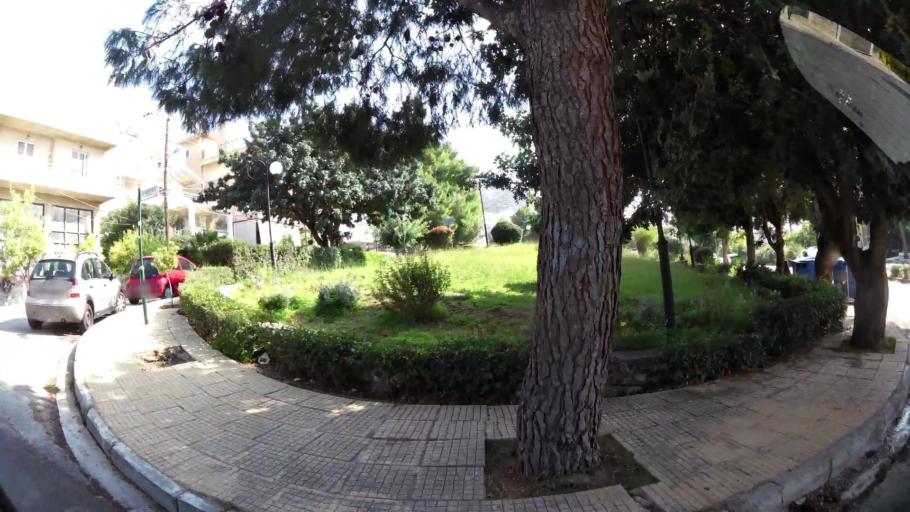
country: GR
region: Attica
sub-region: Nomarchia Athinas
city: Ilioupoli
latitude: 37.9229
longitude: 23.7612
